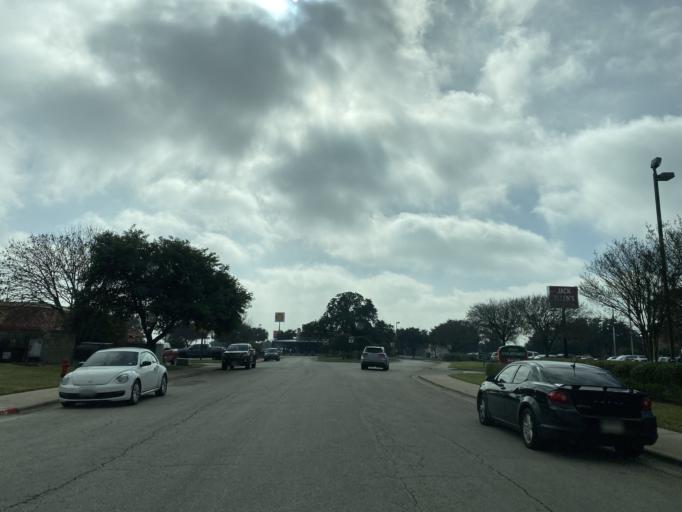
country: US
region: Texas
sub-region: Williamson County
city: Round Rock
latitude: 30.5387
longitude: -97.6937
